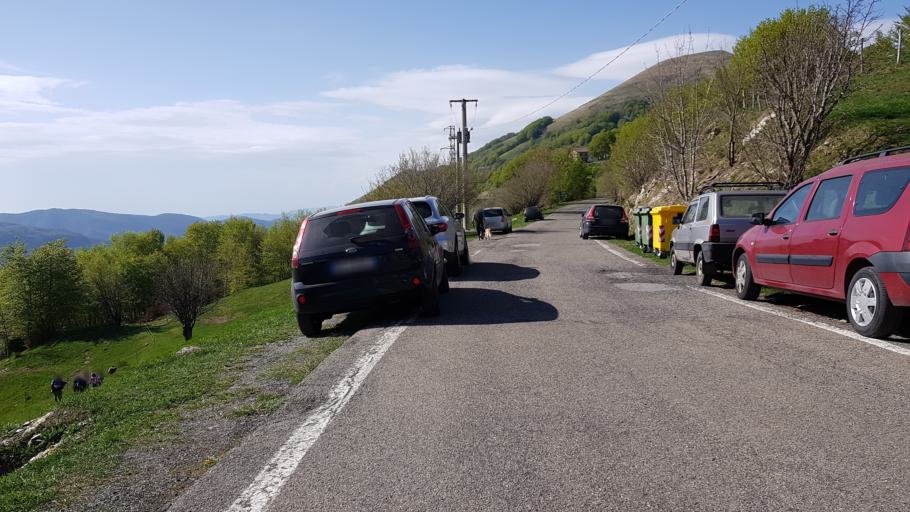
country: IT
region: Liguria
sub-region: Provincia di Genova
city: Fascia
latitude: 44.6016
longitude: 9.2047
